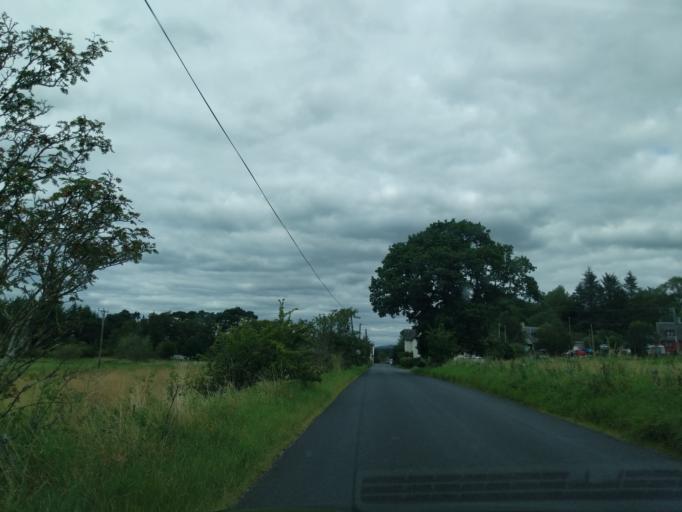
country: GB
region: Scotland
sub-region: The Scottish Borders
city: West Linton
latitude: 55.7169
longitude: -3.3374
